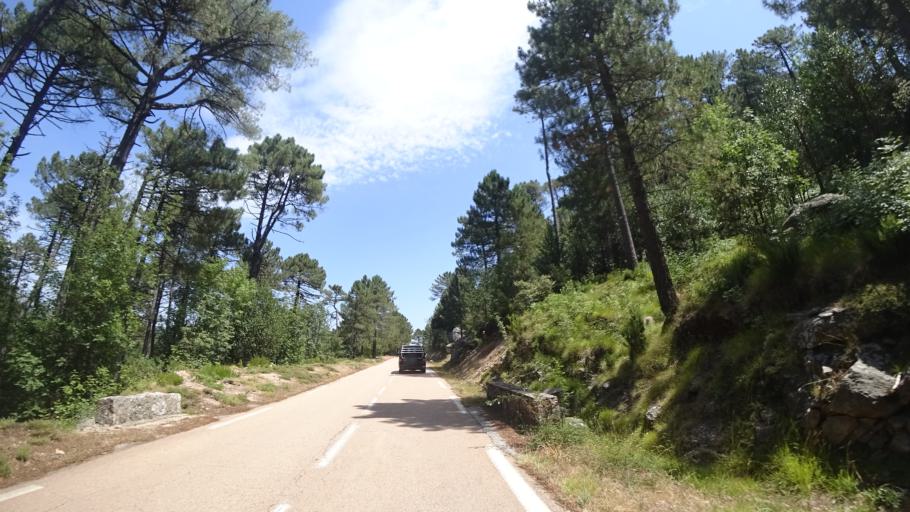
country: FR
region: Corsica
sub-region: Departement de la Corse-du-Sud
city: Zonza
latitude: 41.6766
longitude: 9.2019
